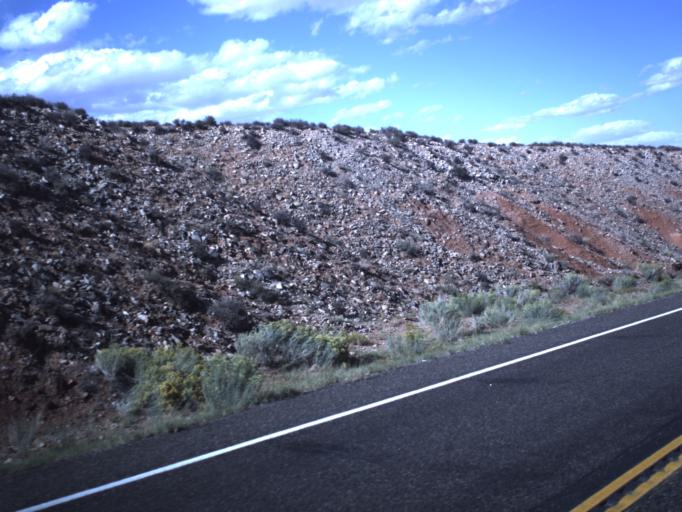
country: US
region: Utah
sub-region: Wayne County
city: Loa
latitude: 38.1275
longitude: -110.6149
